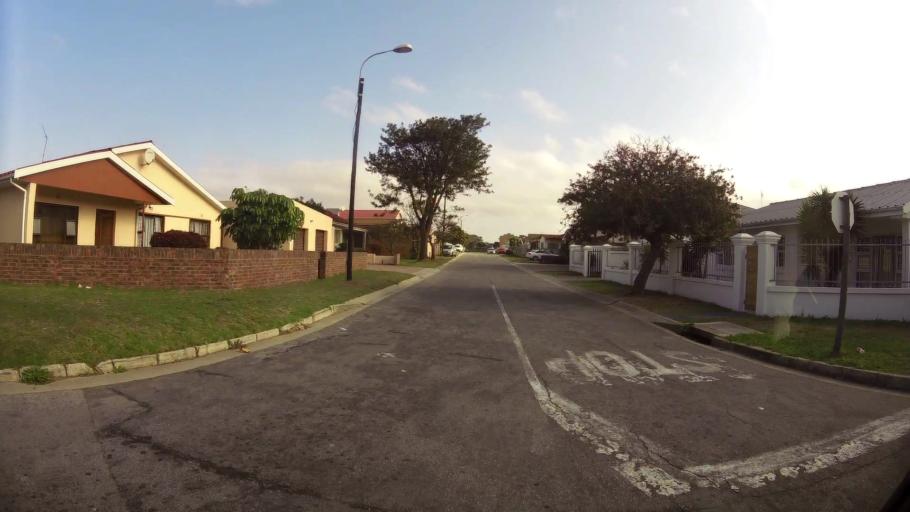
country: ZA
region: Eastern Cape
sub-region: Nelson Mandela Bay Metropolitan Municipality
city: Port Elizabeth
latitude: -33.9208
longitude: 25.5619
